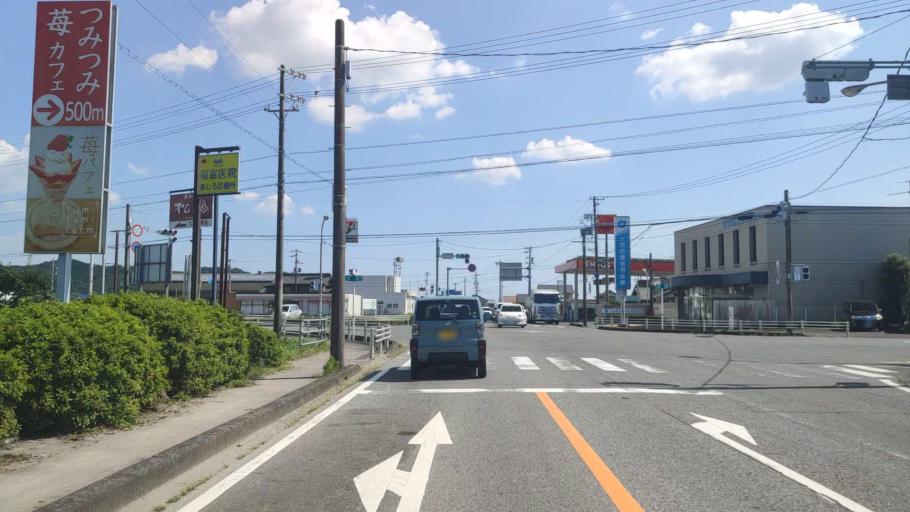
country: JP
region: Gifu
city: Godo
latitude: 35.4864
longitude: 136.6736
